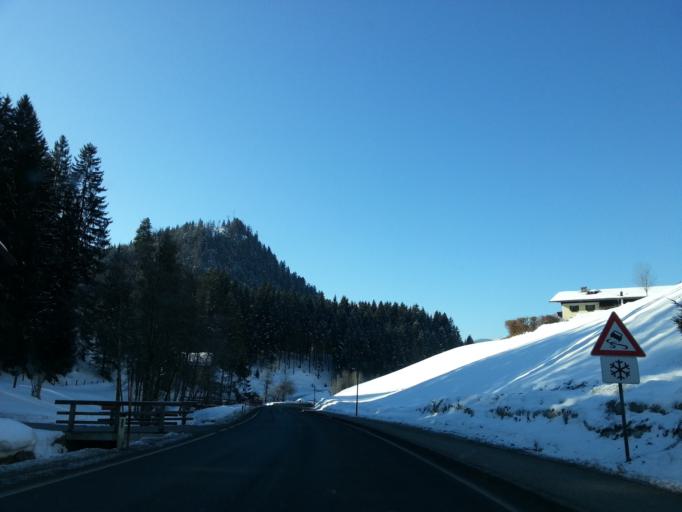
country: AT
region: Salzburg
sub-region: Politischer Bezirk Sankt Johann im Pongau
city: Eben im Pongau
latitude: 47.4588
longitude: 13.3748
